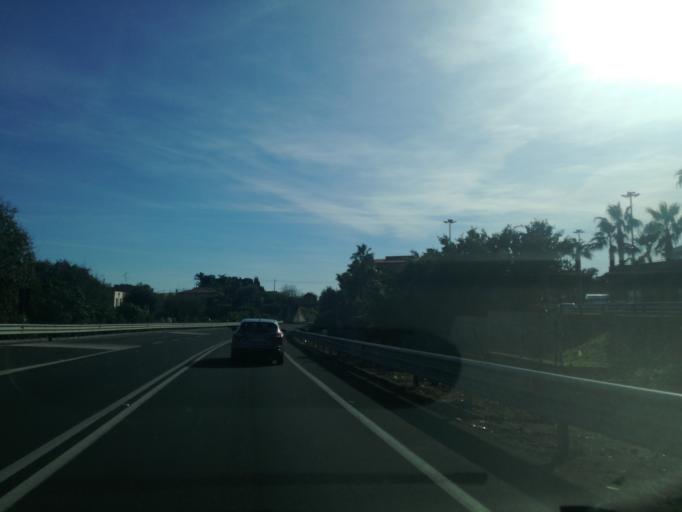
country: IT
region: Sicily
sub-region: Catania
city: Vambolieri
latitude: 37.5960
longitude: 15.1681
